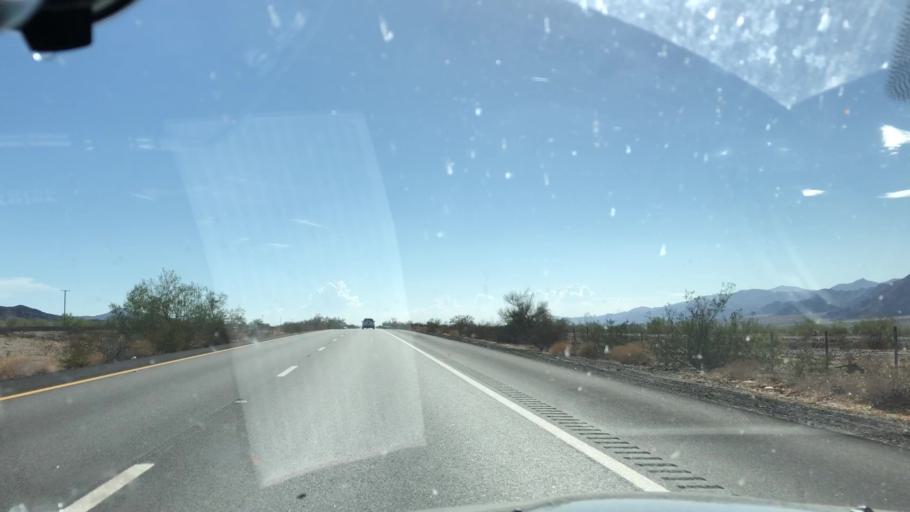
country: US
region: California
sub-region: Imperial County
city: Niland
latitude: 33.6985
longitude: -115.4717
